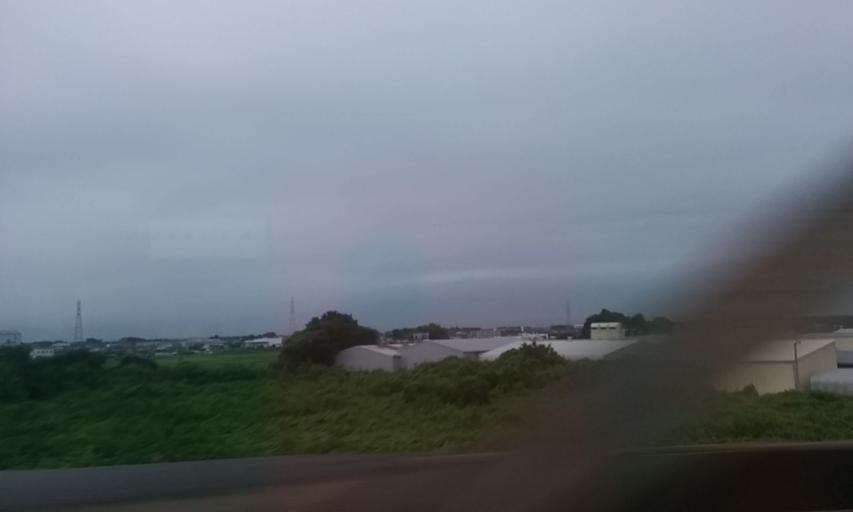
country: JP
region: Ibaraki
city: Koga
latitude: 36.1574
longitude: 139.7295
